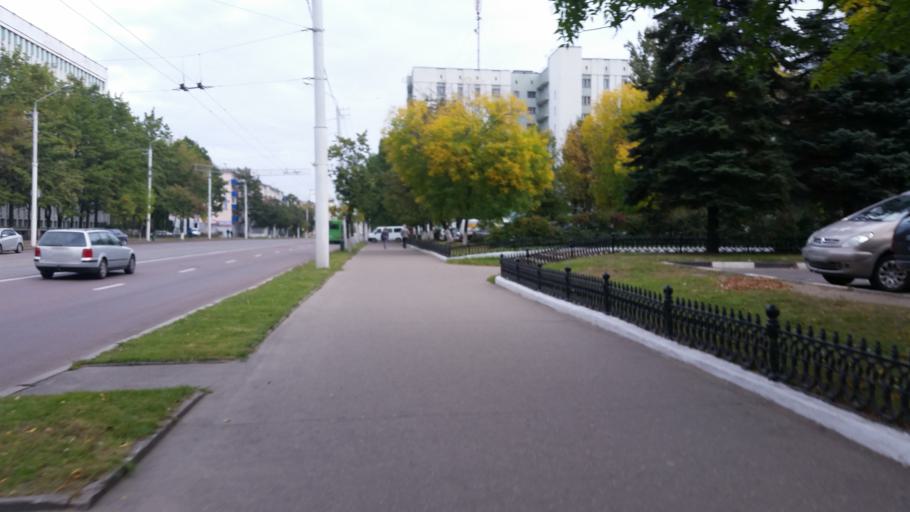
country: BY
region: Vitebsk
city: Vitebsk
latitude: 55.1747
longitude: 30.2002
